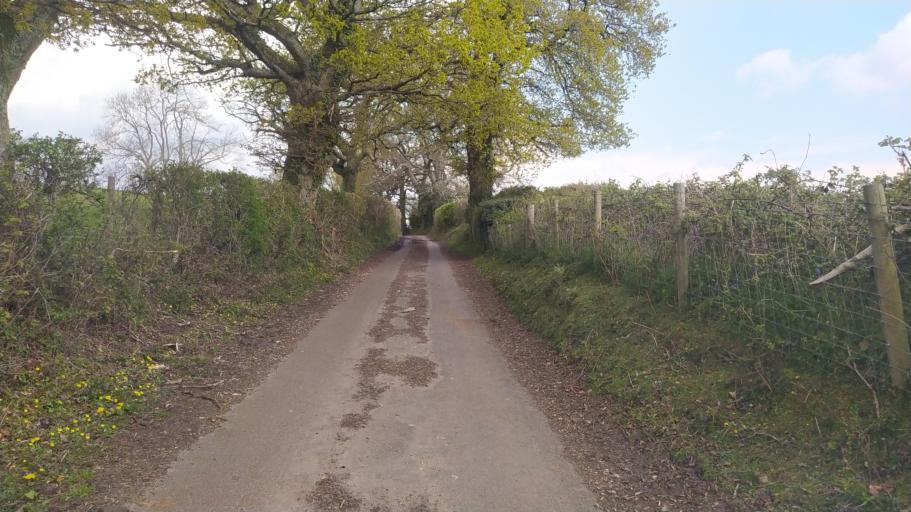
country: GB
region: England
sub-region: Hampshire
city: Cadnam
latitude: 50.9413
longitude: -1.6136
